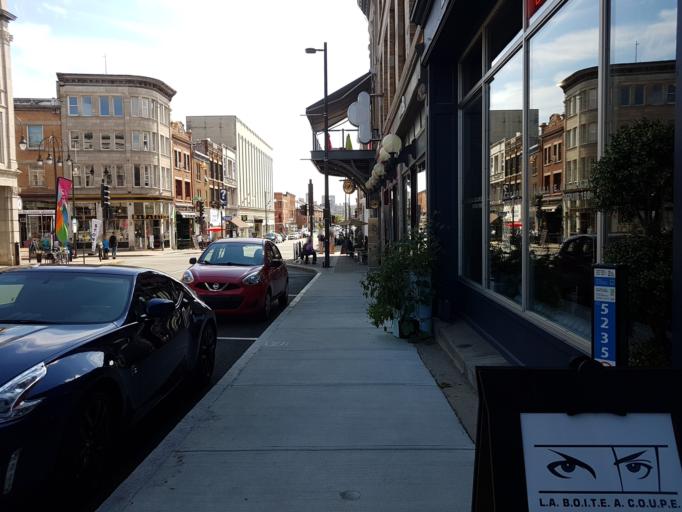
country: CA
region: Quebec
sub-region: Mauricie
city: Trois-Rivieres
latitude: 46.3422
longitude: -72.5403
